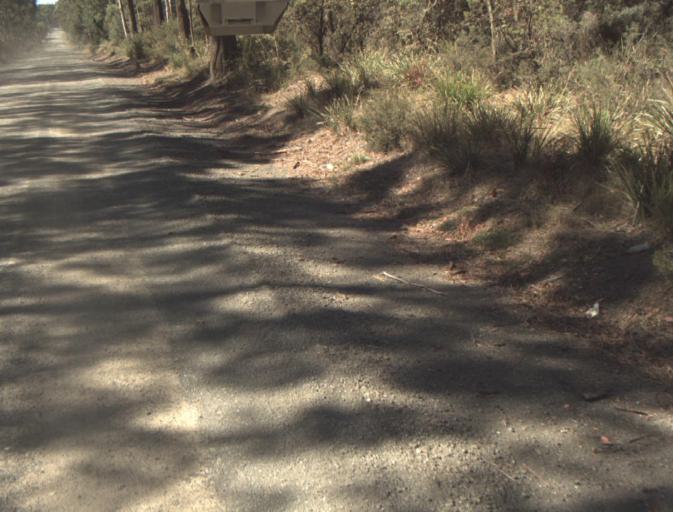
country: AU
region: Tasmania
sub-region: Launceston
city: Mayfield
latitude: -41.3444
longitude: 147.2136
